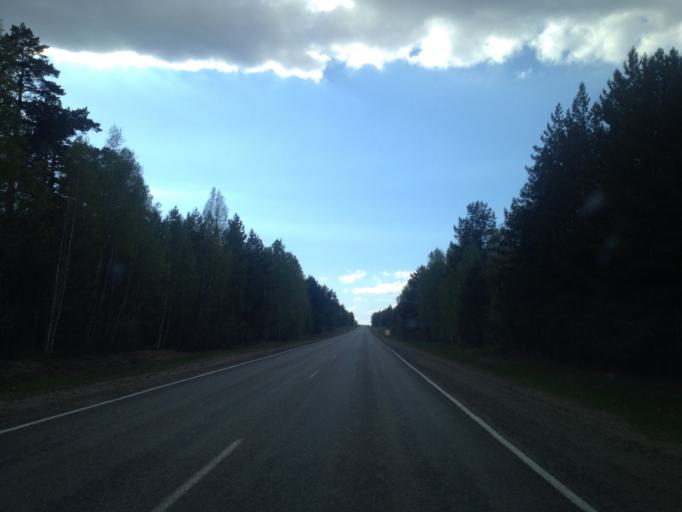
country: RU
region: Kurgan
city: Krasnyy Oktyabr'
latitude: 55.9341
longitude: 64.5180
